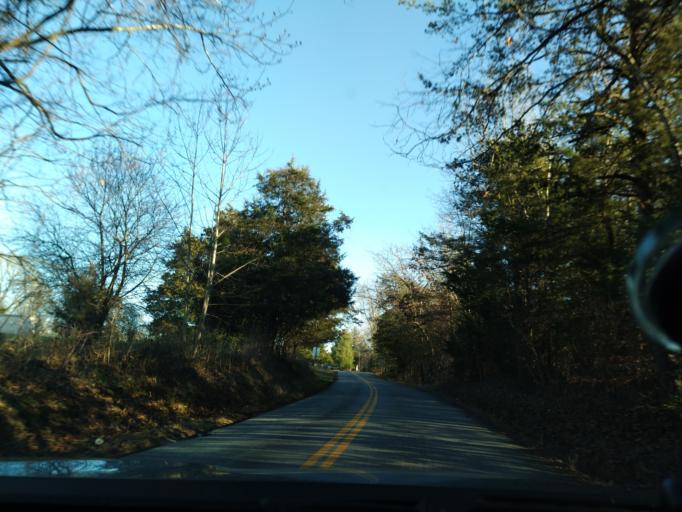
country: US
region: Virginia
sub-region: Prince Edward County
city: Hampden Sydney
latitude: 37.3079
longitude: -78.5629
